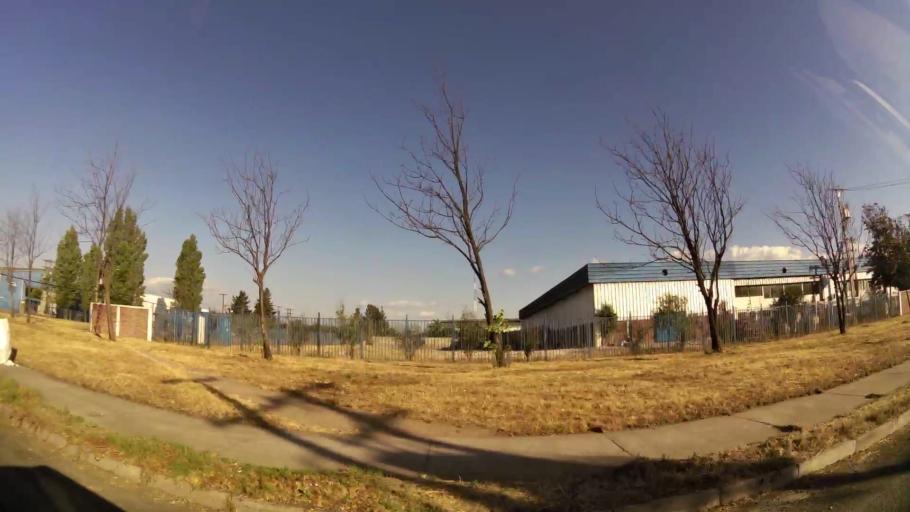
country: CL
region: Santiago Metropolitan
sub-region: Provincia de Maipo
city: San Bernardo
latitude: -33.5329
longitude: -70.7504
